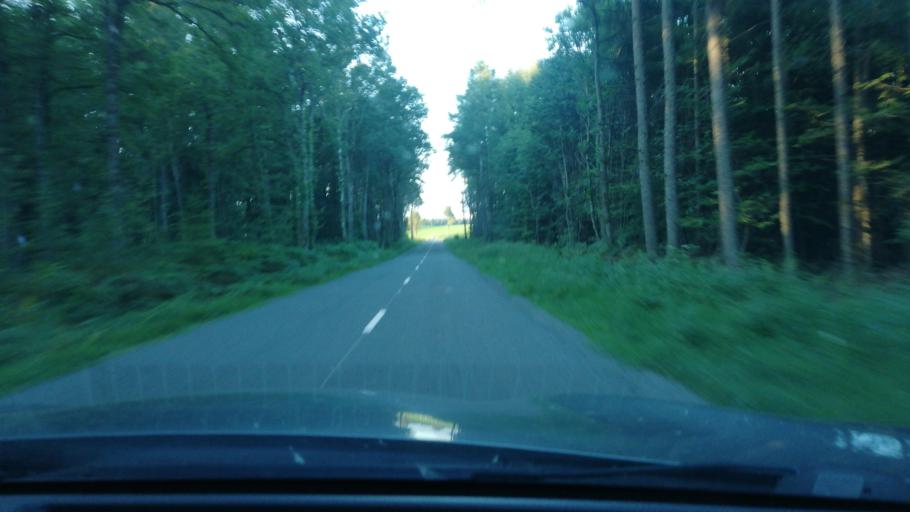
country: FR
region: Auvergne
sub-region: Departement du Cantal
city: Laroquebrou
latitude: 44.9078
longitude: 2.0561
